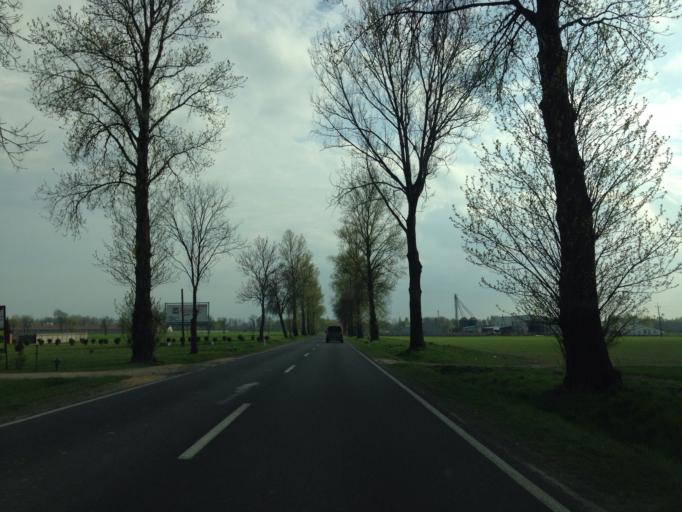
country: PL
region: Masovian Voivodeship
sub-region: Powiat zurominski
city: Zuromin
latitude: 53.0342
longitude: 19.9126
